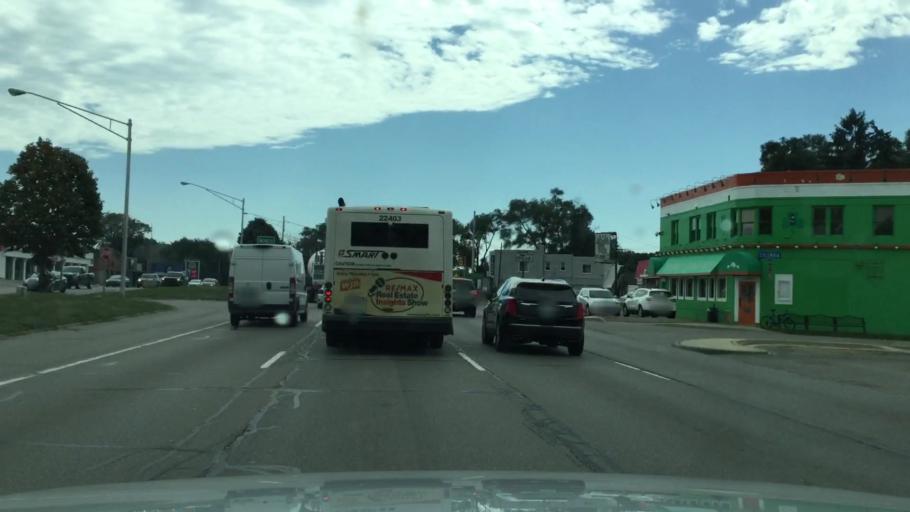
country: US
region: Michigan
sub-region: Oakland County
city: Huntington Woods
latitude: 42.4914
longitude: -83.1608
